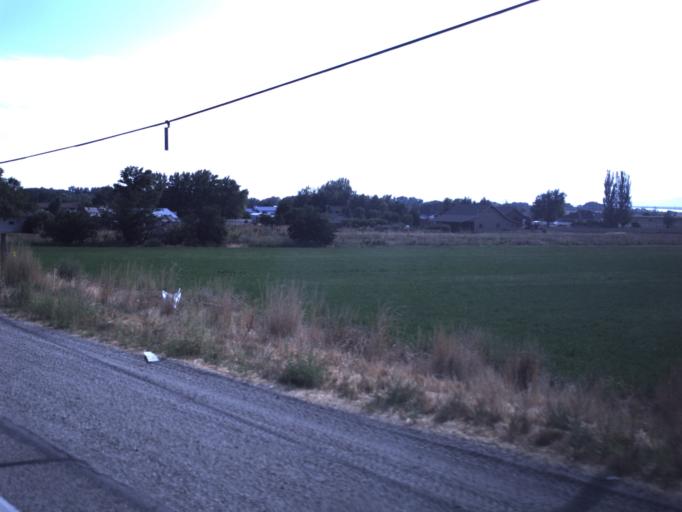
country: US
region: Utah
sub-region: Box Elder County
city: Willard
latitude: 41.4306
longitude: -112.0356
